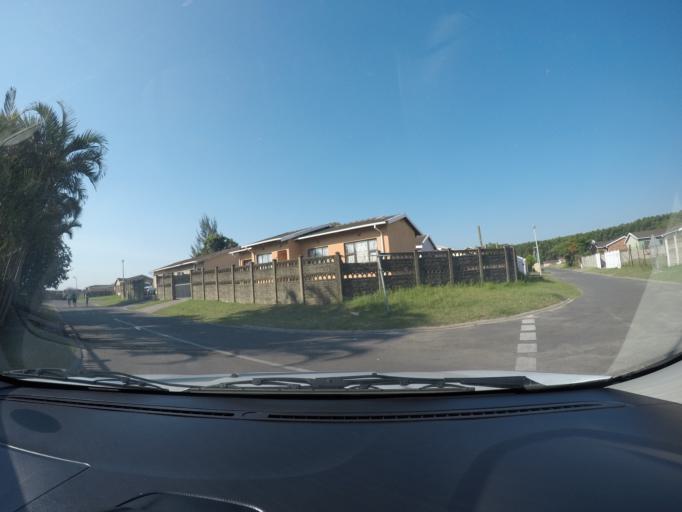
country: ZA
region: KwaZulu-Natal
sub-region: uThungulu District Municipality
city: Richards Bay
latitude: -28.7140
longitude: 32.0404
